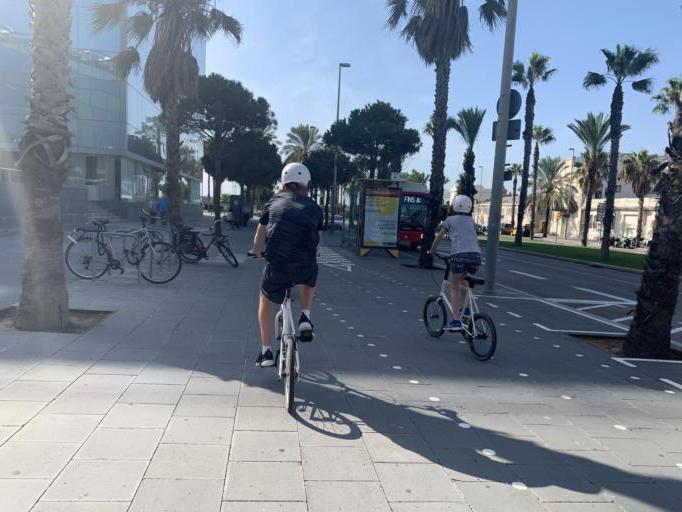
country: ES
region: Catalonia
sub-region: Provincia de Barcelona
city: Ciutat Vella
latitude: 41.3694
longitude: 2.1881
